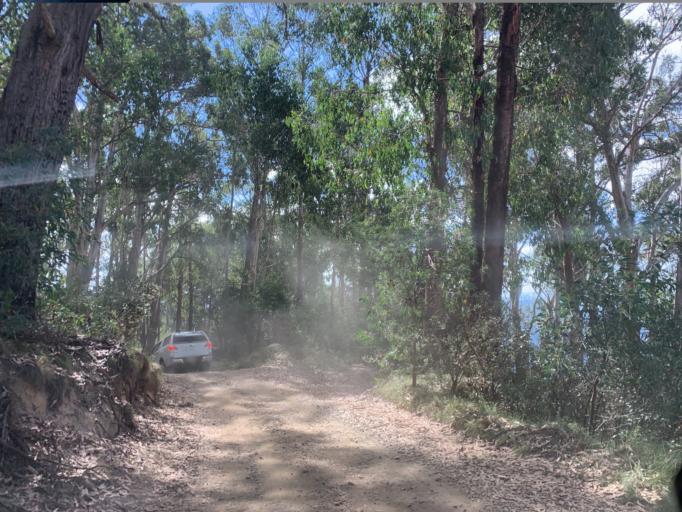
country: AU
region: Victoria
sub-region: Mansfield
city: Mansfield
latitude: -37.0987
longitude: 146.5440
